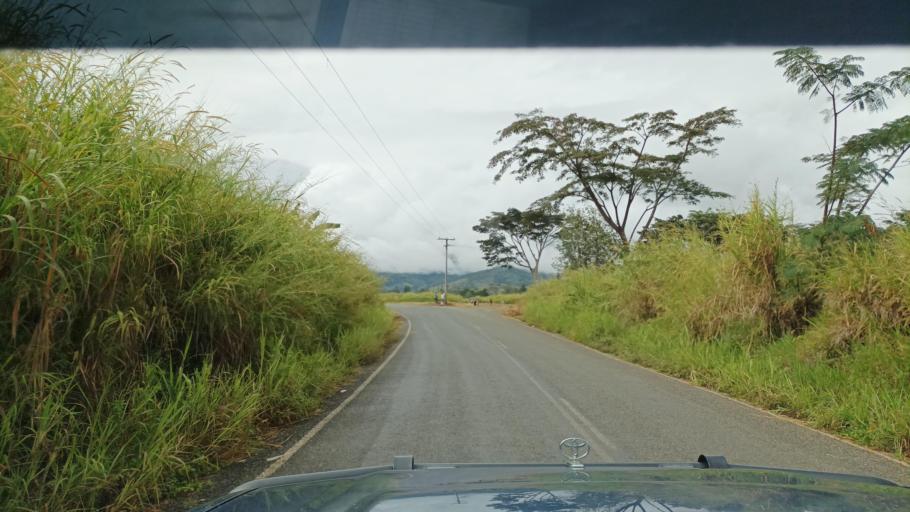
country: PG
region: Jiwaka
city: Minj
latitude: -5.8955
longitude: 144.6822
